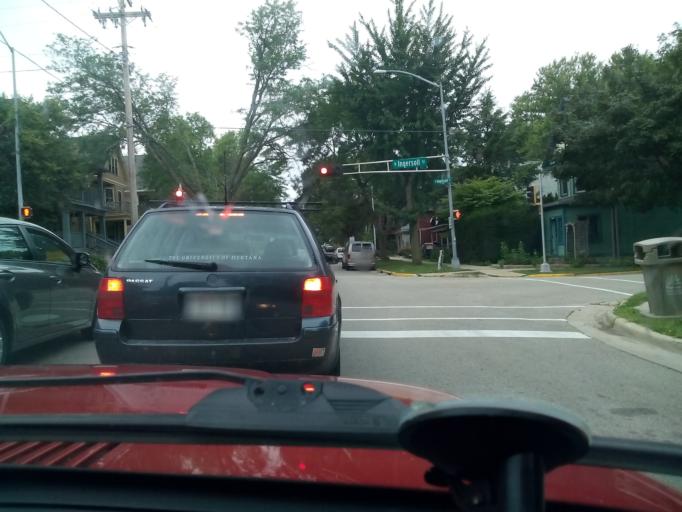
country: US
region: Wisconsin
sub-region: Dane County
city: Maple Bluff
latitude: 43.0878
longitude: -89.3732
